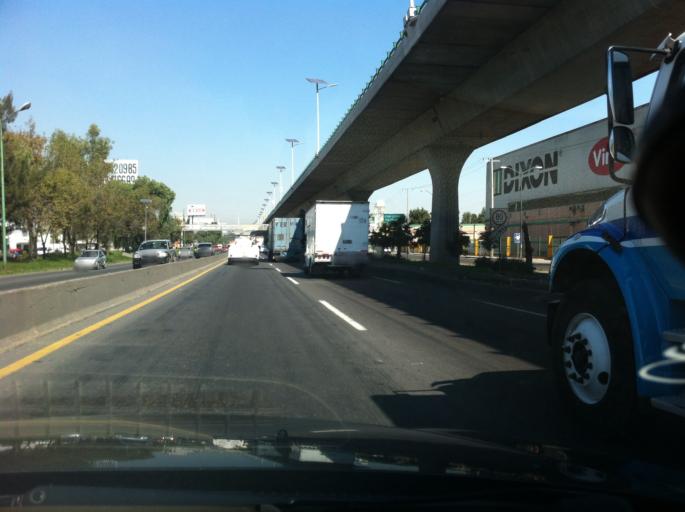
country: MX
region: Mexico
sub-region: Tultitlan
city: Buenavista
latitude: 19.6098
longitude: -99.1900
